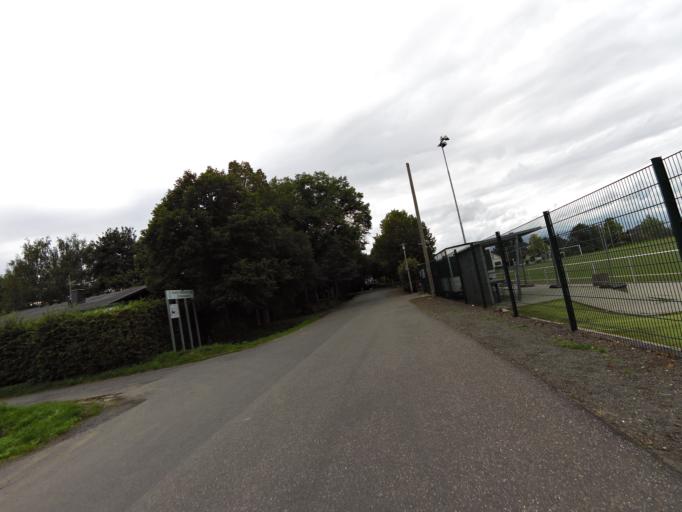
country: DE
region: North Rhine-Westphalia
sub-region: Regierungsbezirk Koln
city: Rheinbach
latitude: 50.6040
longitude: 6.9829
